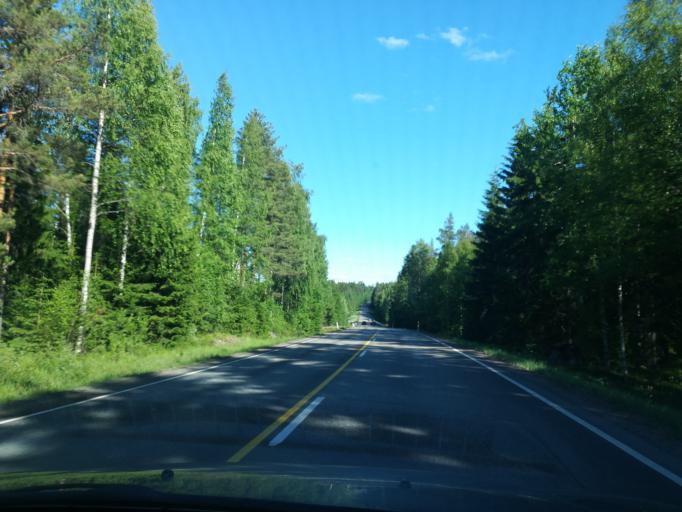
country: FI
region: South Karelia
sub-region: Imatra
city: Ruokolahti
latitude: 61.3591
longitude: 28.7060
